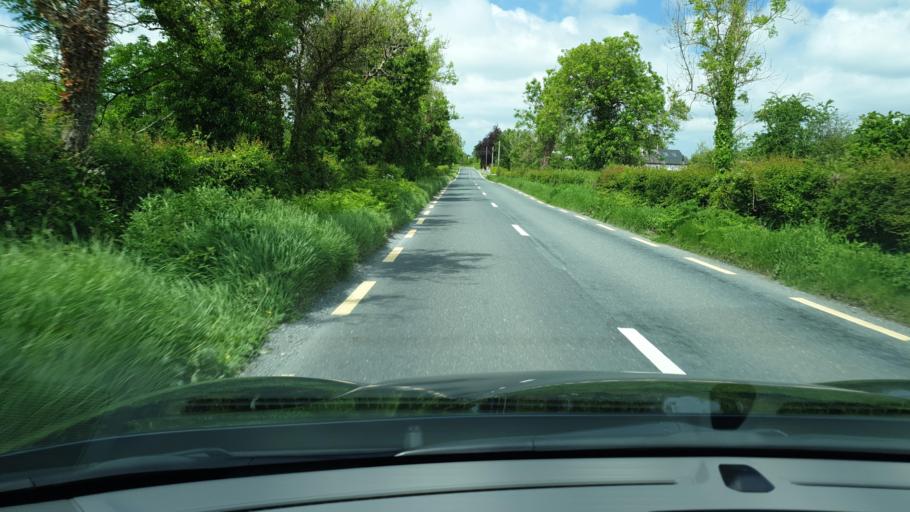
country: IE
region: Ulster
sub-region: An Cabhan
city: Kingscourt
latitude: 53.8911
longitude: -6.7553
